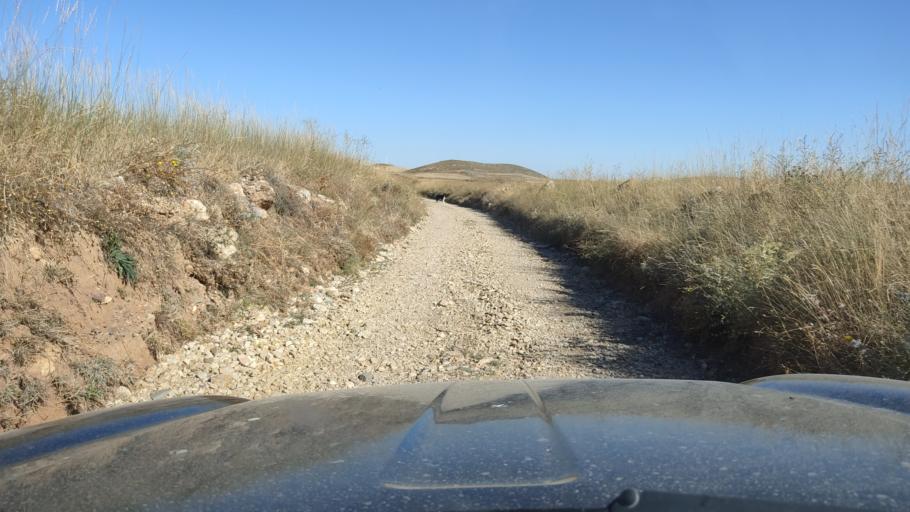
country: ES
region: Aragon
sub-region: Provincia de Teruel
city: Monforte de Moyuela
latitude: 41.0392
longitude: -0.9994
